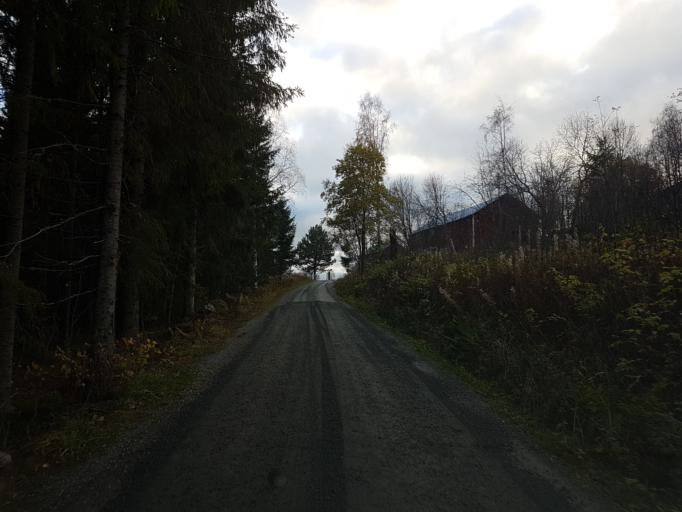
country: SE
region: Vaesternorrland
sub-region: OErnskoeldsviks Kommun
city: Bjasta
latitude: 63.0740
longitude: 18.4459
